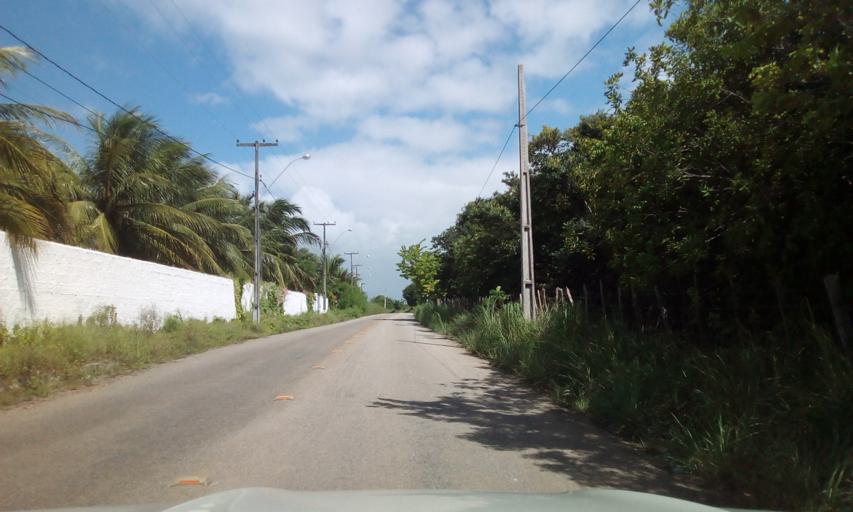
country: BR
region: Paraiba
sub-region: Conde
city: Conde
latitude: -7.2228
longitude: -34.8129
